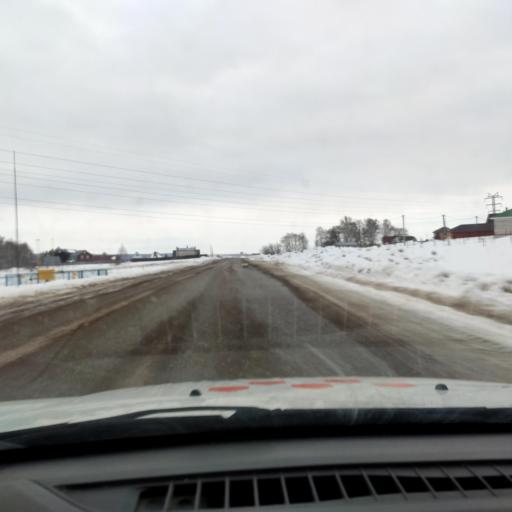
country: RU
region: Bashkortostan
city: Avdon
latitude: 54.6354
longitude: 55.6981
